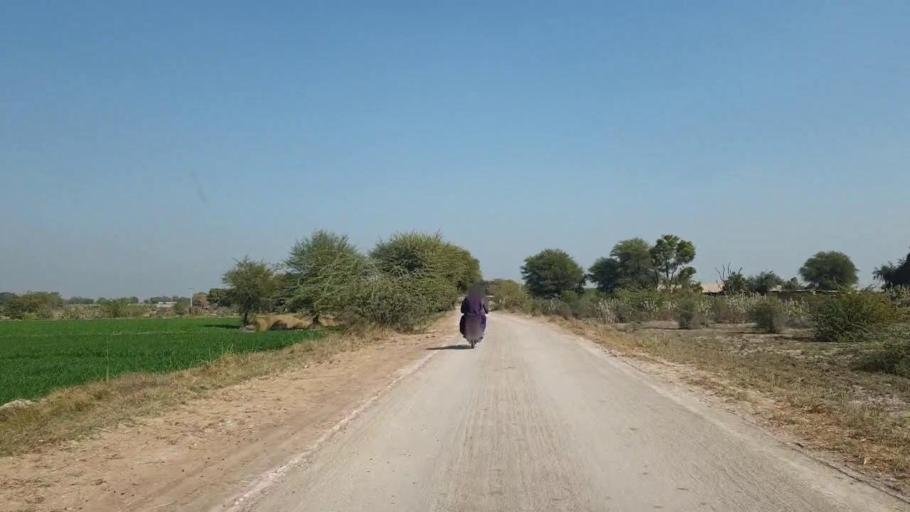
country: PK
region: Sindh
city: Shahdadpur
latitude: 25.9231
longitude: 68.5090
